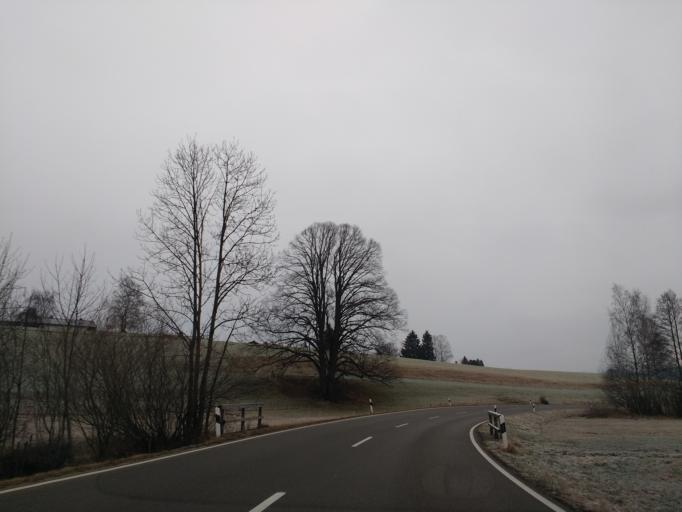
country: AT
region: Tyrol
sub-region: Politischer Bezirk Reutte
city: Vils
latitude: 47.5749
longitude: 10.6434
